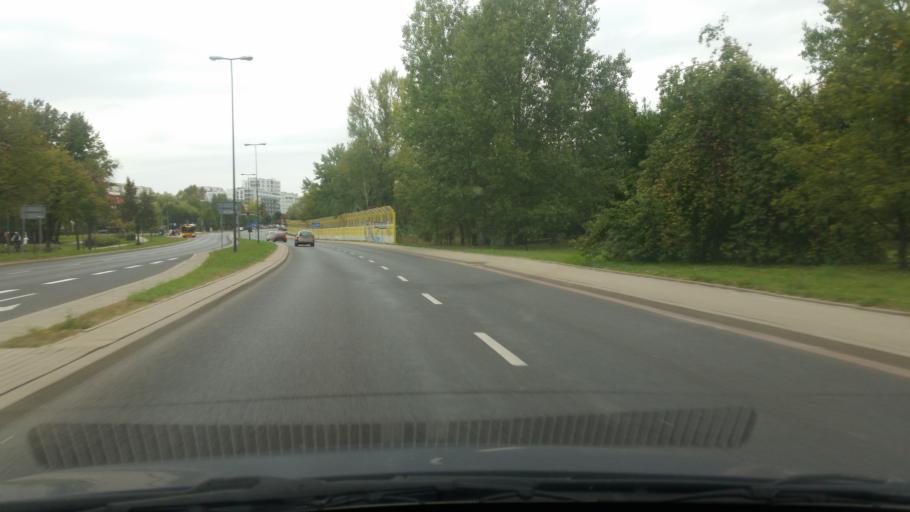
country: PL
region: Masovian Voivodeship
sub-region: Warszawa
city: Kabaty
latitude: 52.1377
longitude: 21.0714
